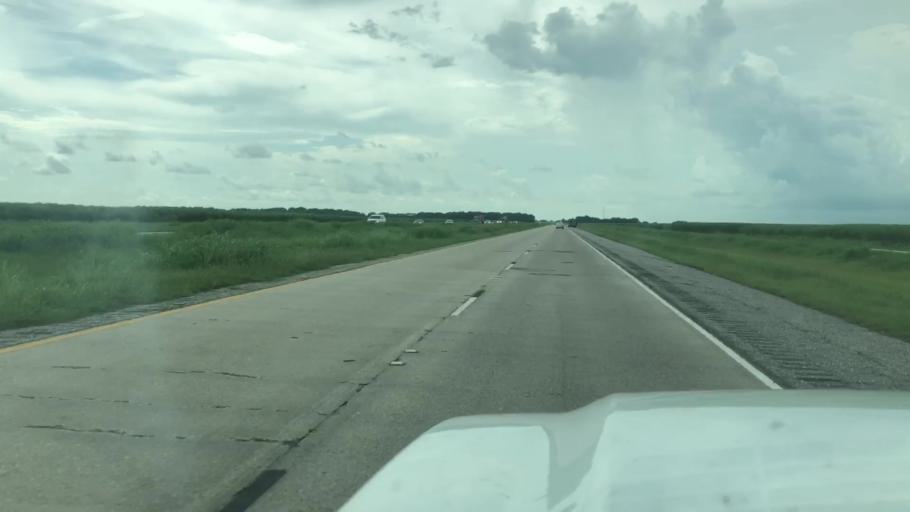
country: US
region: Louisiana
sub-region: Saint Mary Parish
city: Baldwin
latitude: 29.8485
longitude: -91.5923
